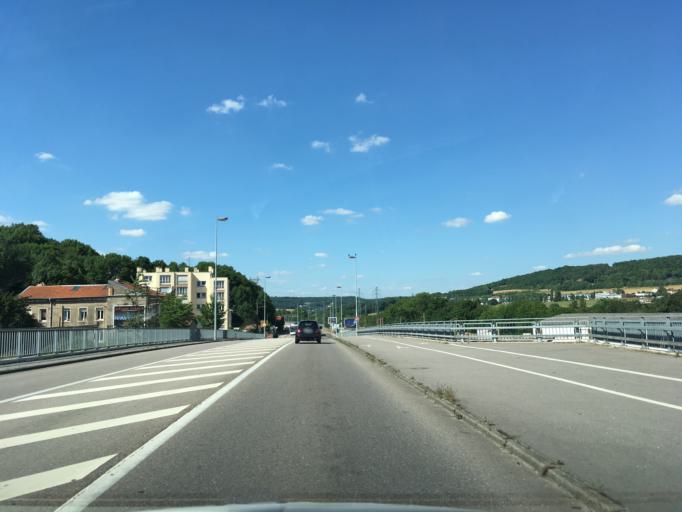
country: FR
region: Lorraine
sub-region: Departement de Meurthe-et-Moselle
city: Maxeville
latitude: 48.7192
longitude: 6.1712
